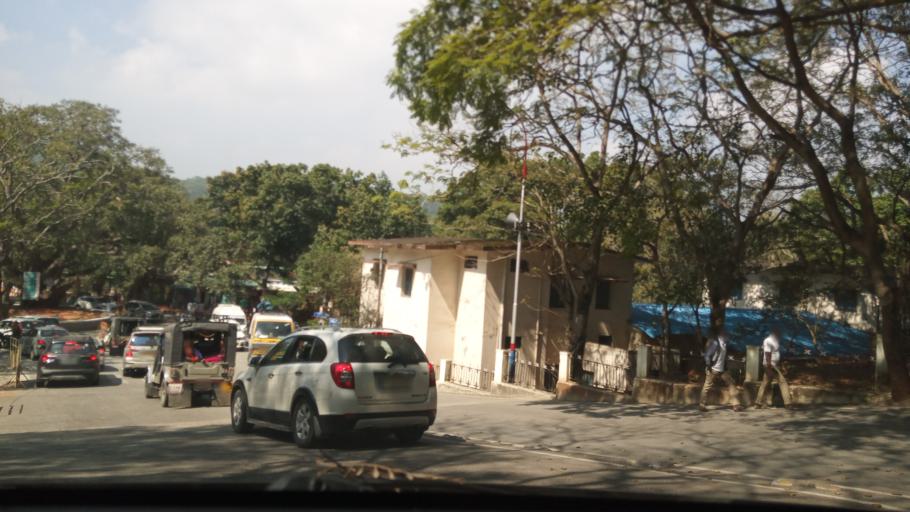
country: IN
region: Andhra Pradesh
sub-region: Chittoor
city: Tirumala
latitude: 13.6782
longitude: 79.3451
